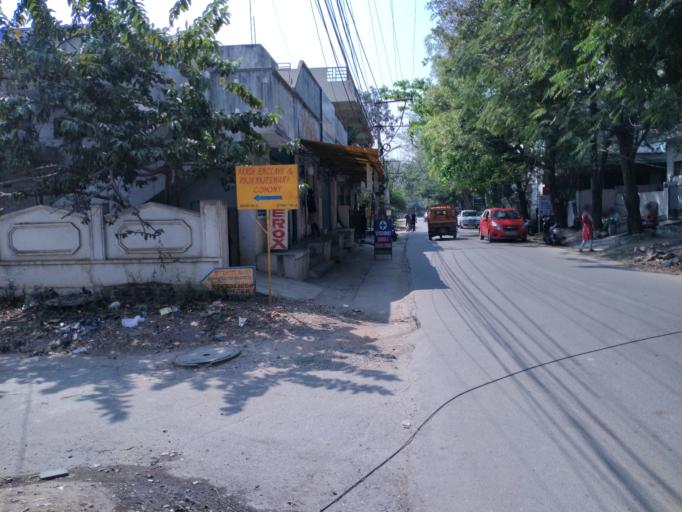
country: IN
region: Telangana
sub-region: Rangareddi
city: Secunderabad
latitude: 17.4981
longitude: 78.5464
